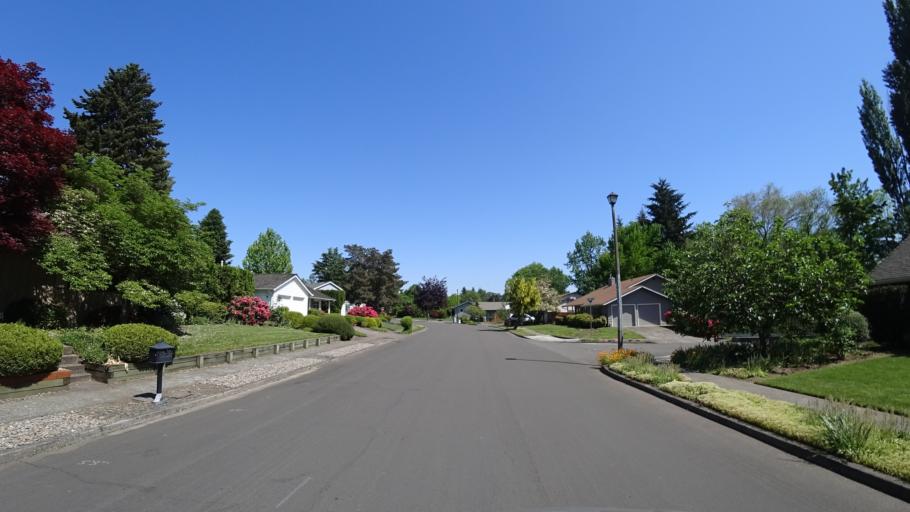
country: US
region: Oregon
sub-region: Washington County
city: Rockcreek
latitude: 45.5470
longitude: -122.8755
